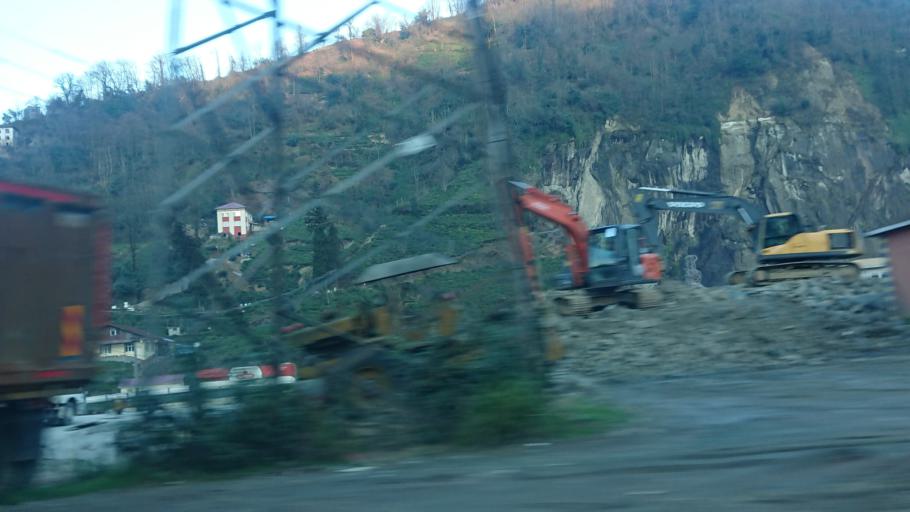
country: TR
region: Rize
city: Gundogdu
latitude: 41.0302
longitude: 40.5823
